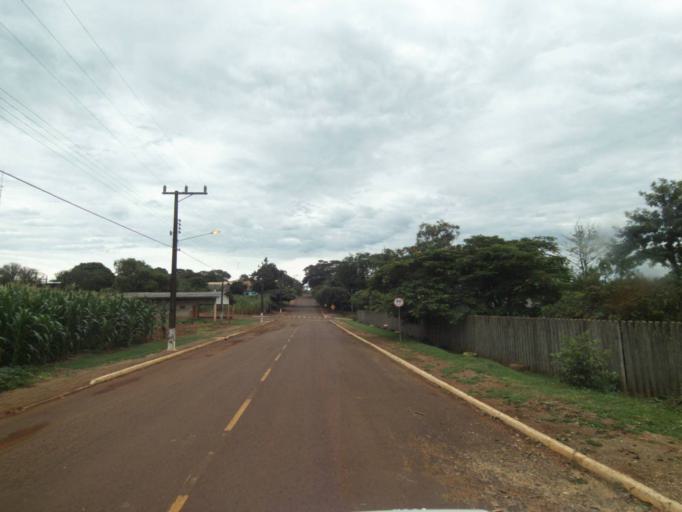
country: BR
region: Parana
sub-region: Guaraniacu
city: Guaraniacu
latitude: -24.9194
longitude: -52.9372
